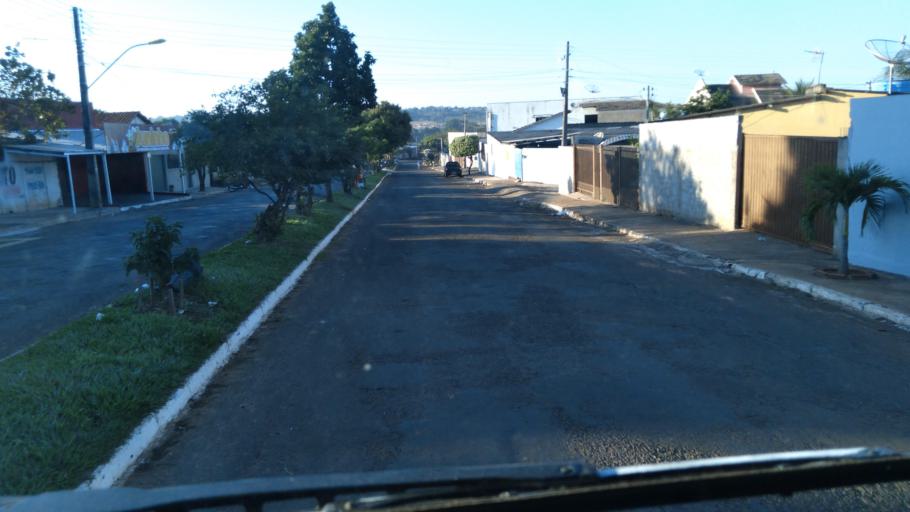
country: BR
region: Goias
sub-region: Mineiros
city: Mineiros
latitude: -17.5733
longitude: -52.5684
